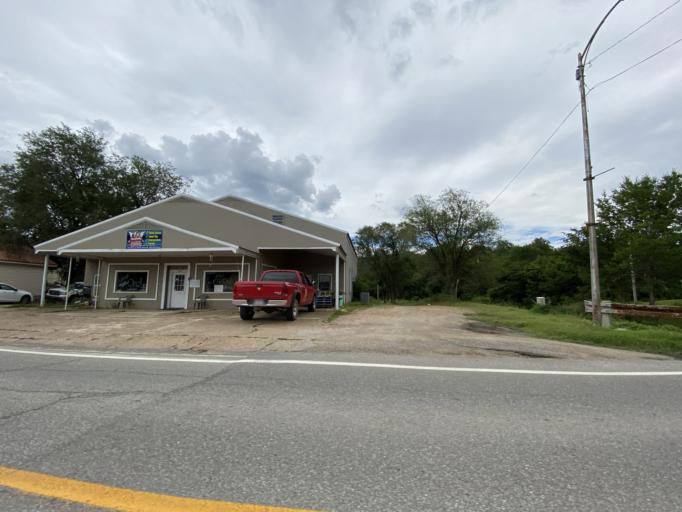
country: US
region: Arkansas
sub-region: Fulton County
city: Salem
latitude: 36.3699
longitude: -91.8227
